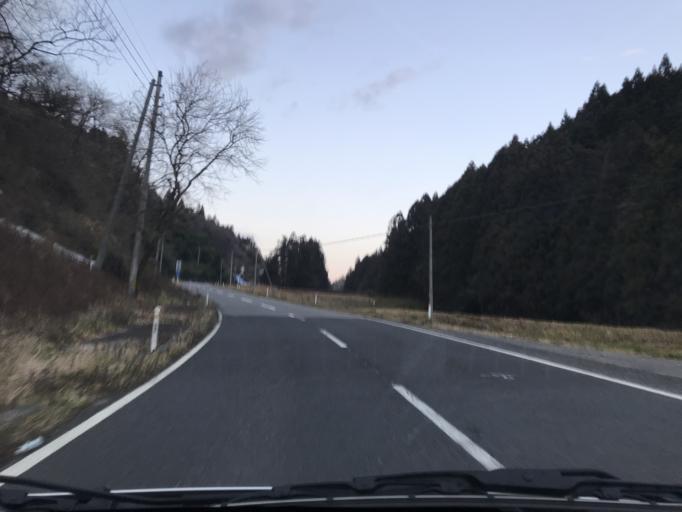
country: JP
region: Iwate
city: Ichinoseki
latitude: 38.8206
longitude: 141.1174
